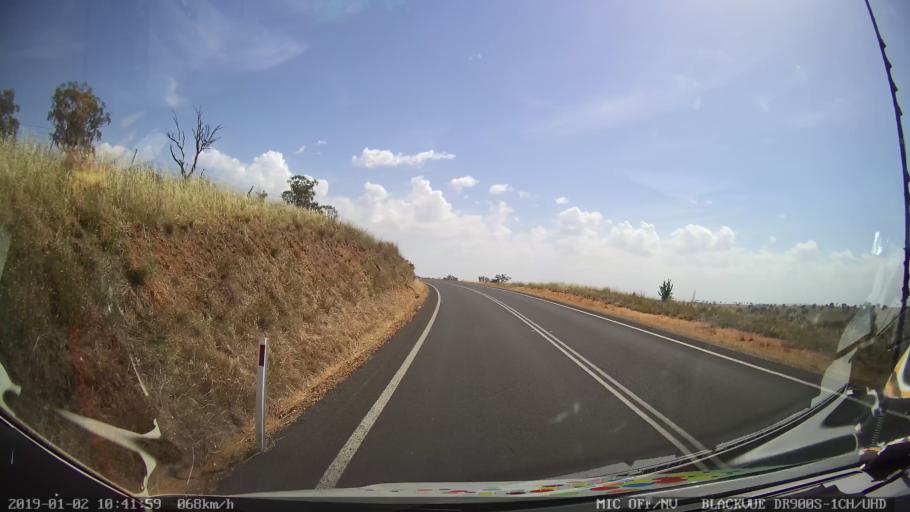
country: AU
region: New South Wales
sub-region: Cootamundra
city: Cootamundra
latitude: -34.7893
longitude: 148.3083
